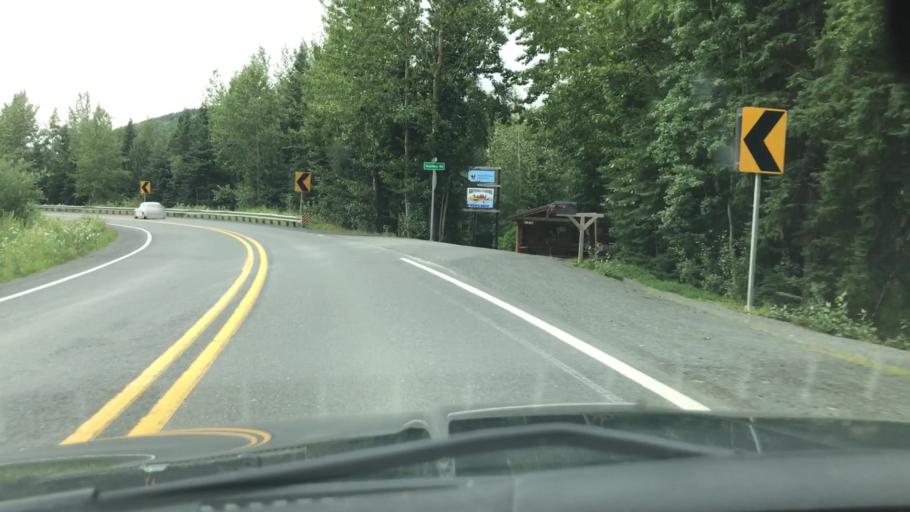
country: US
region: Alaska
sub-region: Kenai Peninsula Borough
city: Seward
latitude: 60.4870
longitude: -149.8726
